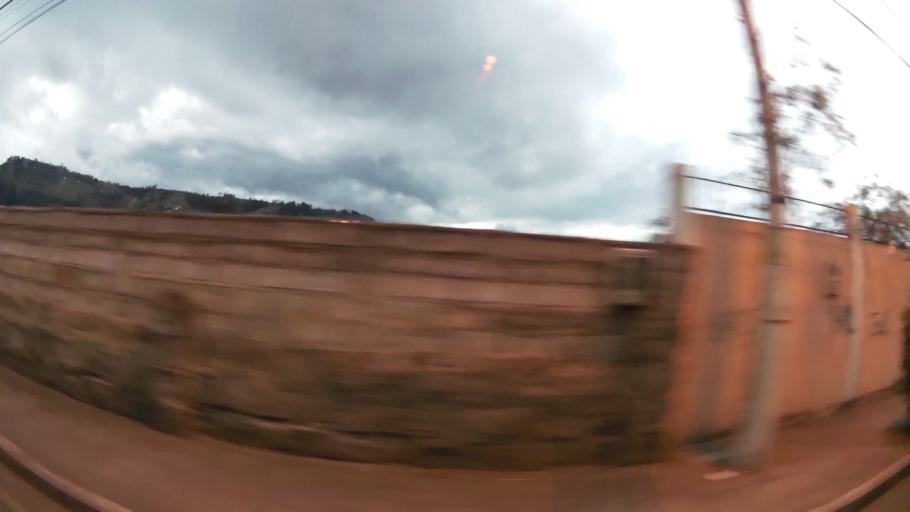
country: EC
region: Tungurahua
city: Ambato
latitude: -1.2497
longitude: -78.6373
